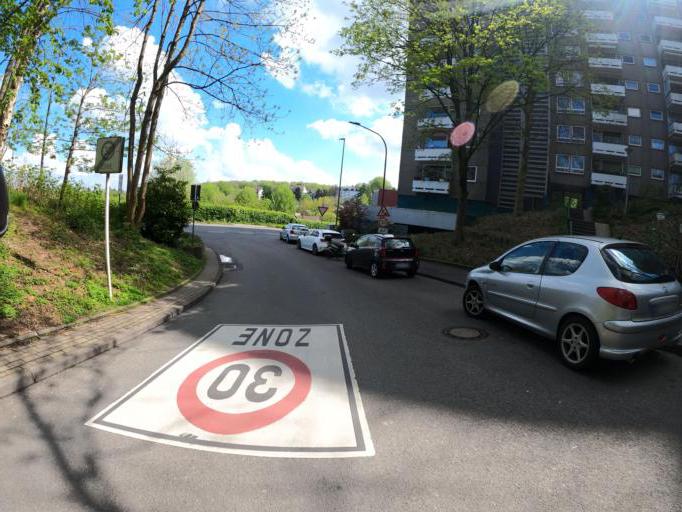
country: DE
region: North Rhine-Westphalia
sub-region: Regierungsbezirk Dusseldorf
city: Wuppertal
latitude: 51.2391
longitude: 7.1527
